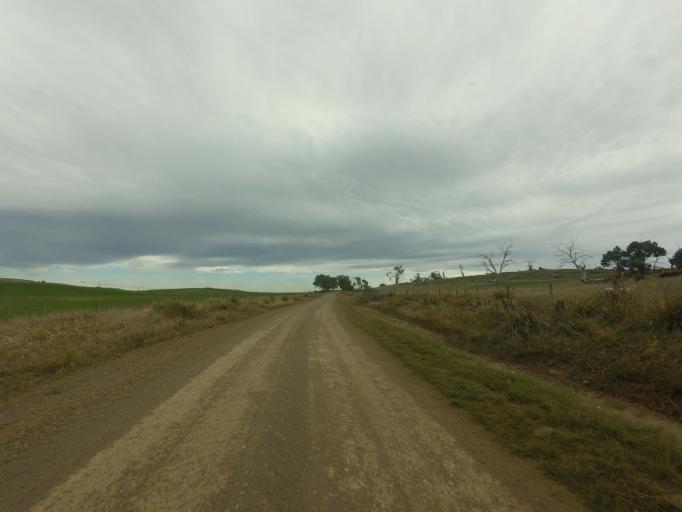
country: AU
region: Tasmania
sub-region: Derwent Valley
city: New Norfolk
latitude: -42.3981
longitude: 146.9676
